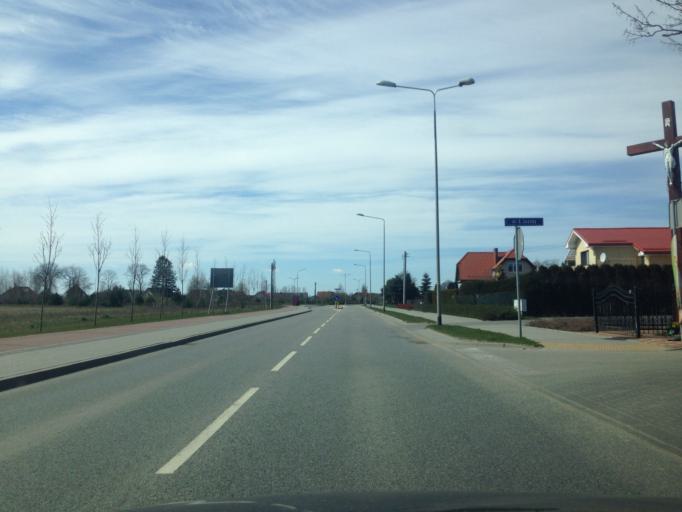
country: PL
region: Pomeranian Voivodeship
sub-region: Powiat kartuski
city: Chwaszczyno
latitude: 54.4987
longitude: 18.4365
